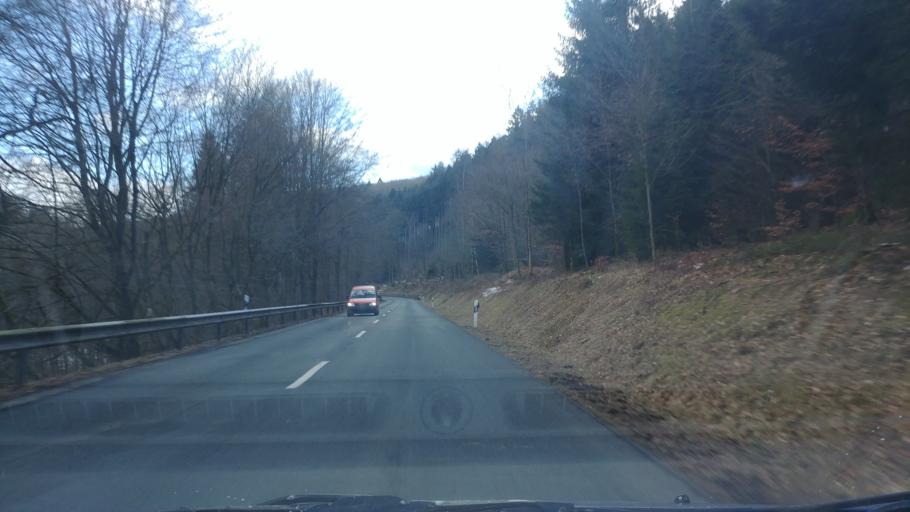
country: DE
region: Lower Saxony
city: Holzminden
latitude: 51.7762
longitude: 9.4785
